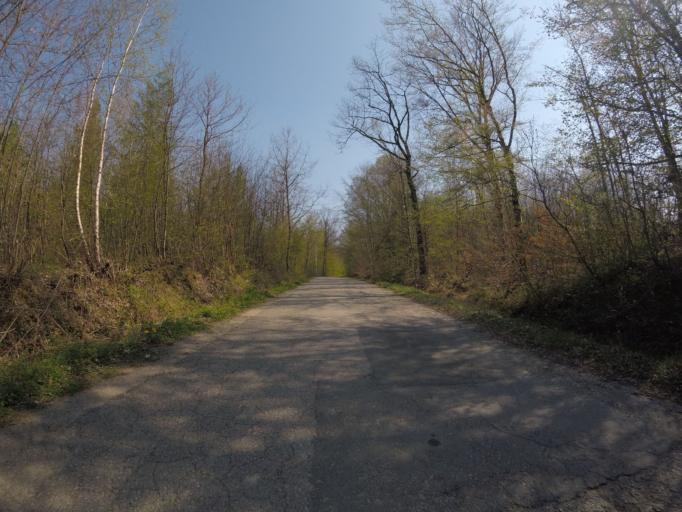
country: HR
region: Grad Zagreb
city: Strmec
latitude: 45.5760
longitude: 15.9203
